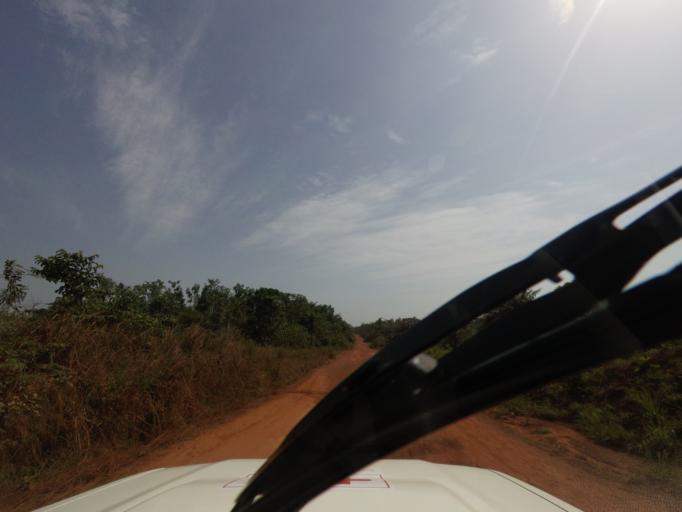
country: LR
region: Bong
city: Gbarnga
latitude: 7.0584
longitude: -9.4658
